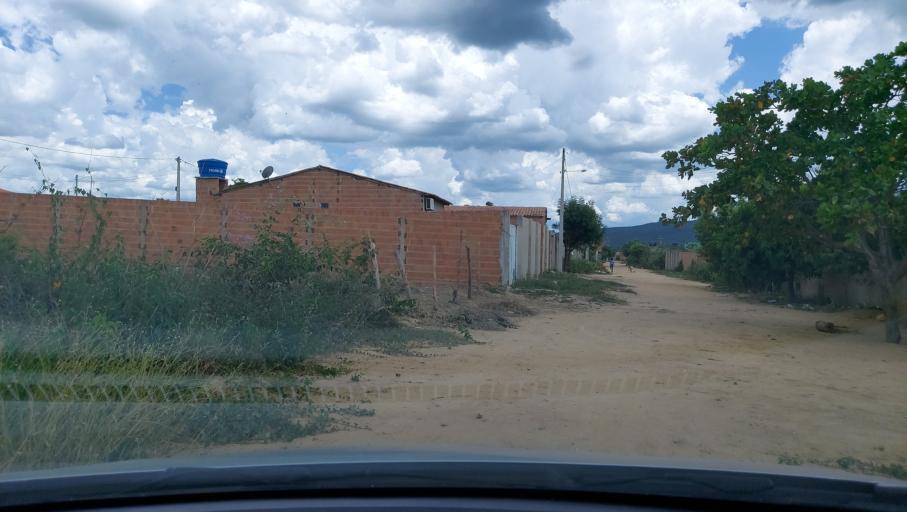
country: BR
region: Bahia
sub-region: Oliveira Dos Brejinhos
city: Beira Rio
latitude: -12.0076
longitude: -42.6326
